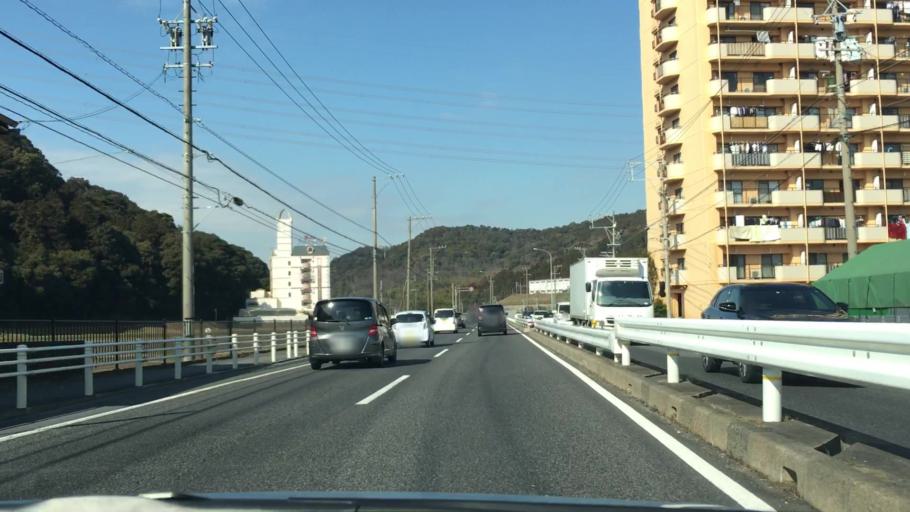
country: JP
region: Aichi
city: Gamagori
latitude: 34.9034
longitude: 137.2352
